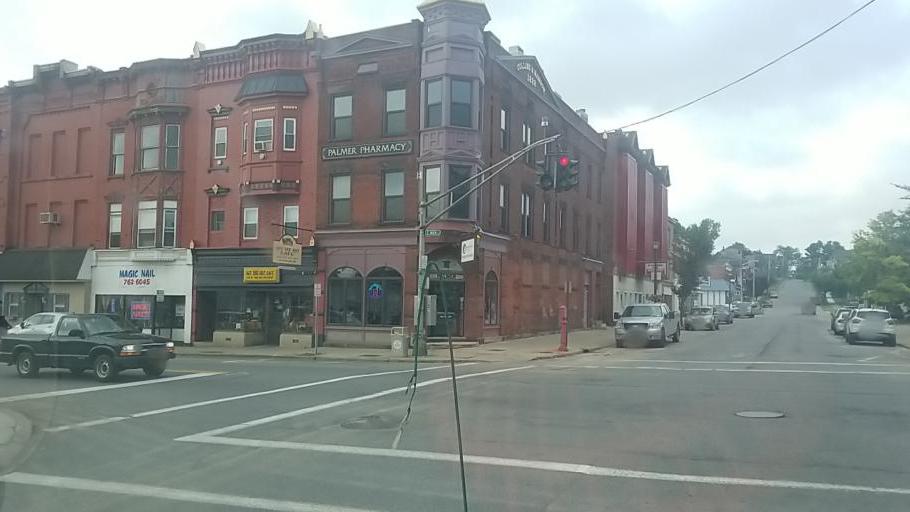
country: US
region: New York
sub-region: Fulton County
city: Johnstown
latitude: 43.0066
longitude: -74.3713
